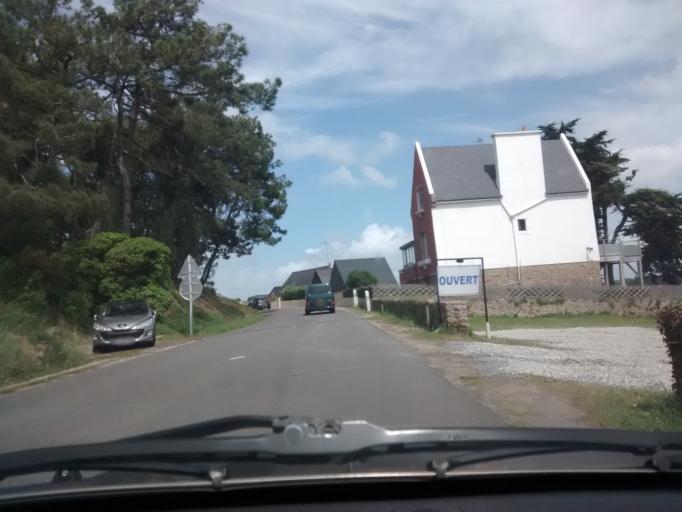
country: FR
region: Brittany
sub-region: Departement du Morbihan
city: Larmor-Baden
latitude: 47.5966
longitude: -2.8925
